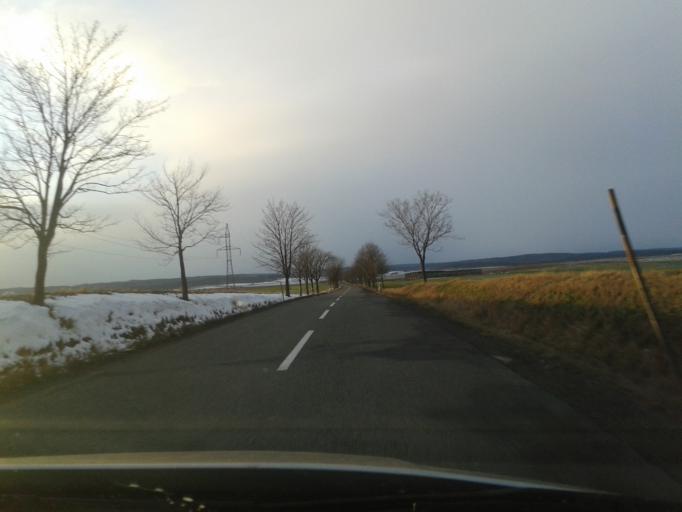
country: CZ
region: Olomoucky
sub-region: Okres Prostejov
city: Plumlov
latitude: 49.4905
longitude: 17.0035
